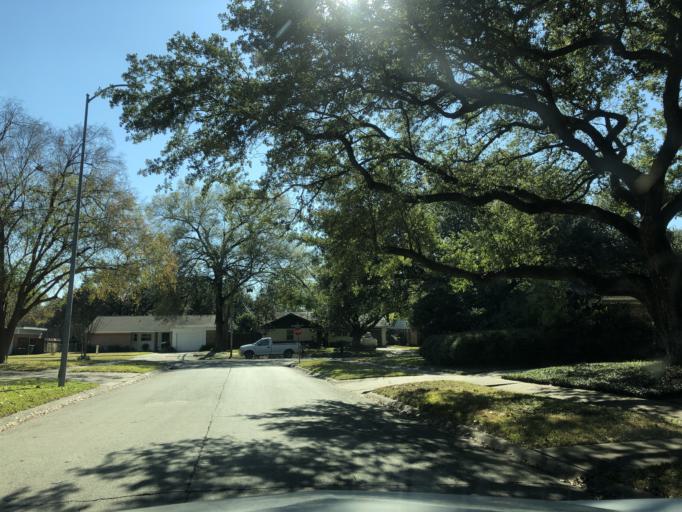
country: US
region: Texas
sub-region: Harris County
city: Bellaire
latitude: 29.6822
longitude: -95.4986
